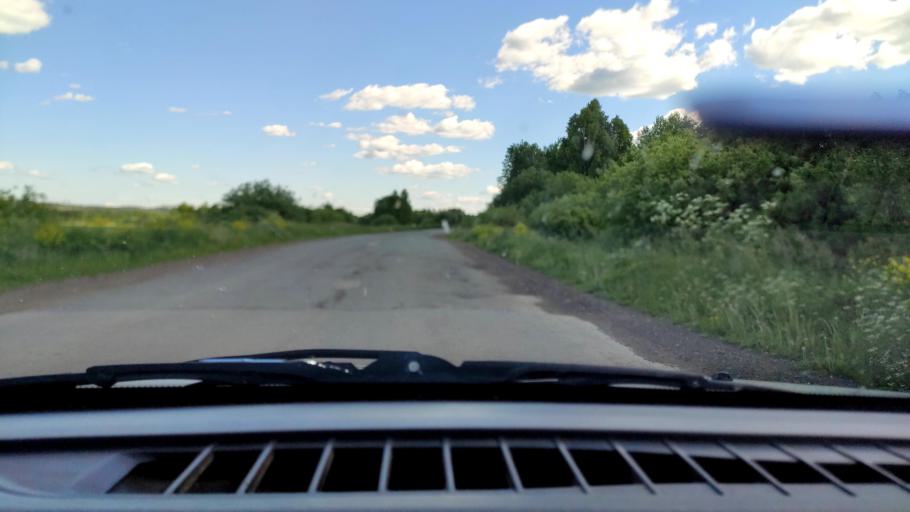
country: RU
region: Perm
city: Uinskoye
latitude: 57.1640
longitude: 56.5688
